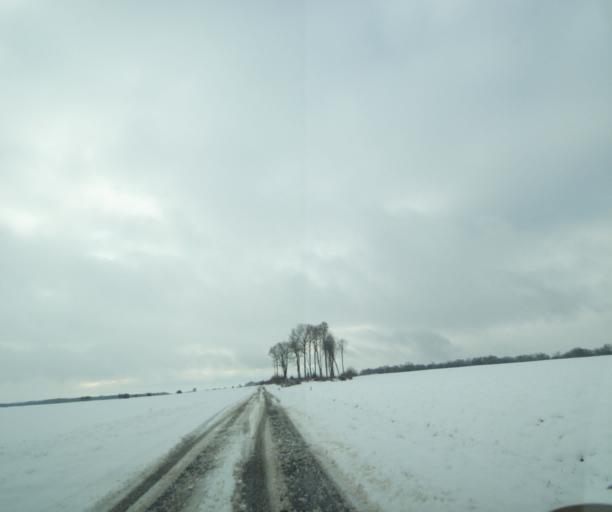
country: FR
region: Champagne-Ardenne
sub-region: Departement de la Haute-Marne
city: Montier-en-Der
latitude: 48.5031
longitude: 4.6863
